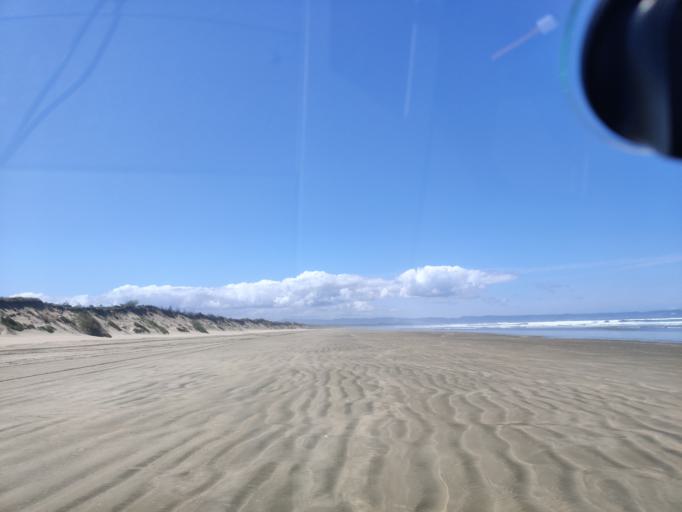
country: NZ
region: Northland
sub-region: Far North District
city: Kaitaia
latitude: -35.0123
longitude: 173.1576
